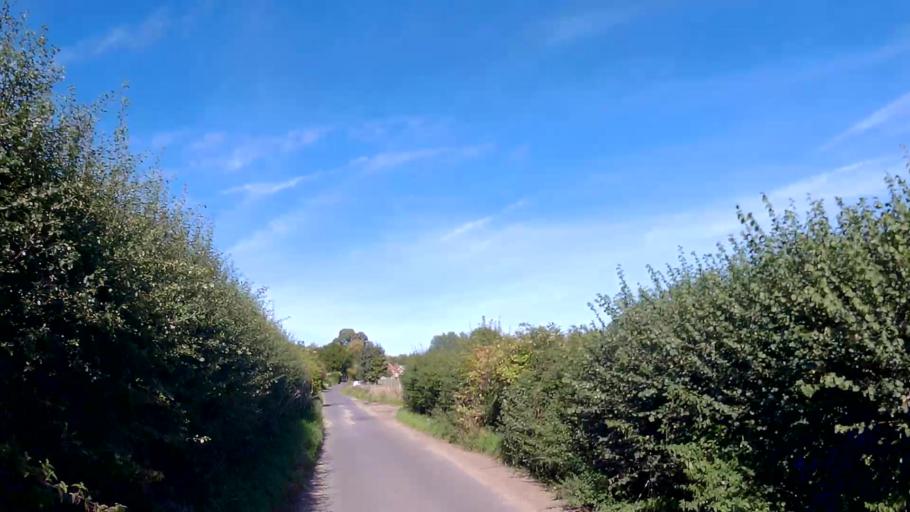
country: GB
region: England
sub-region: Hampshire
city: Andover
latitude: 51.1500
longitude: -1.4629
